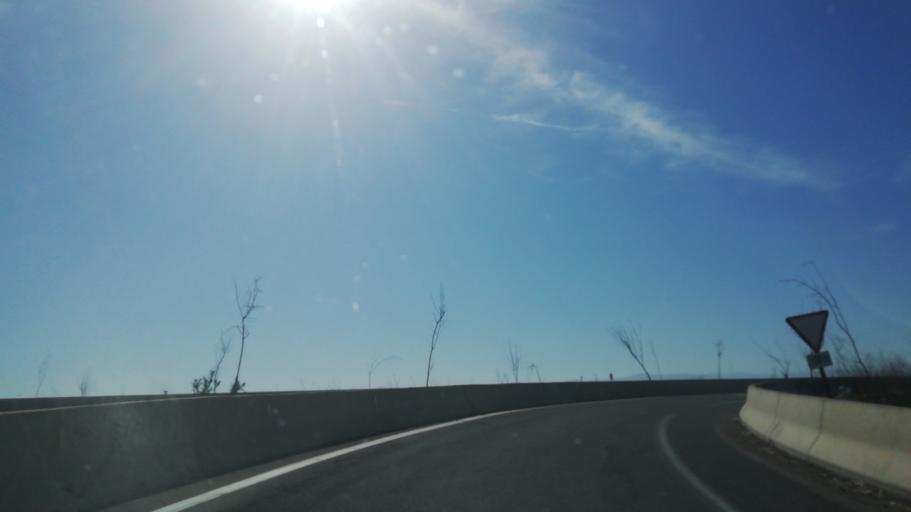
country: DZ
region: Oran
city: Es Senia
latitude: 35.6024
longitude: -0.5734
